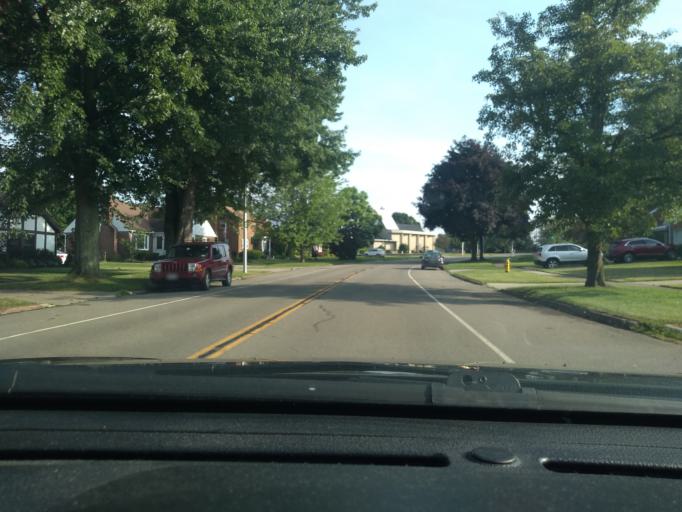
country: US
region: New York
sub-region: Erie County
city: Lackawanna
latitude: 42.8298
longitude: -78.8086
